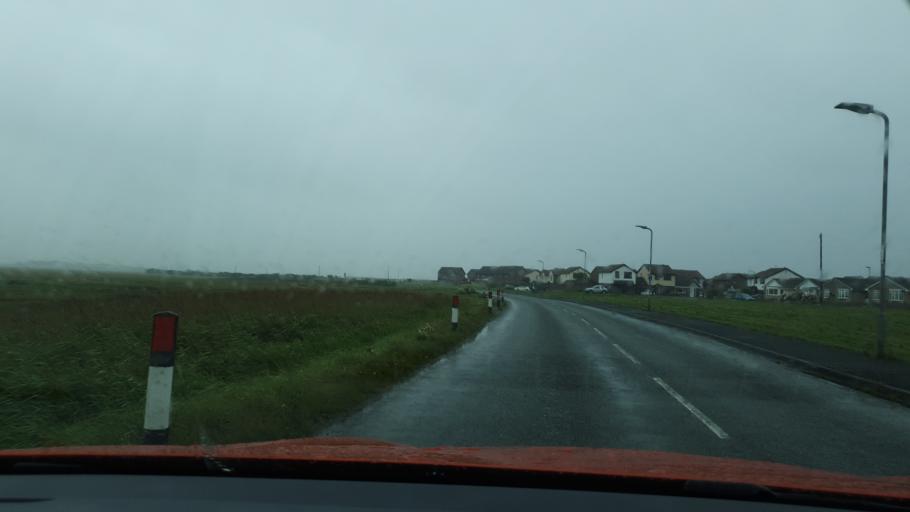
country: GB
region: England
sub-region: Cumbria
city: Barrow in Furness
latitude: 54.0968
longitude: -3.2538
